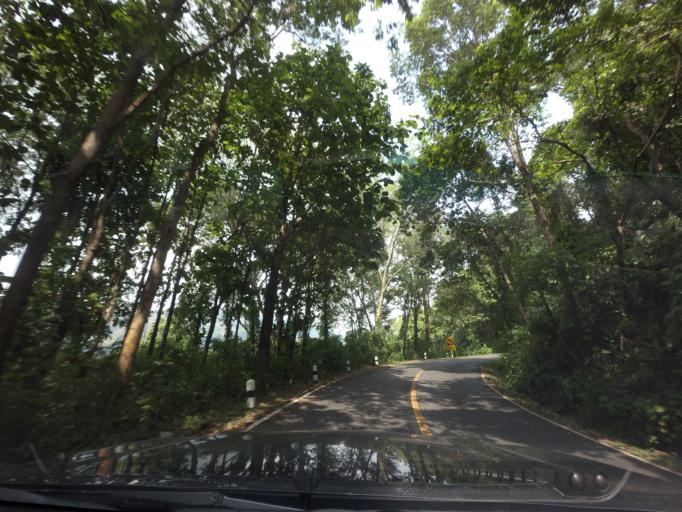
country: TH
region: Nan
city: Pua
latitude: 19.1839
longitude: 100.9963
